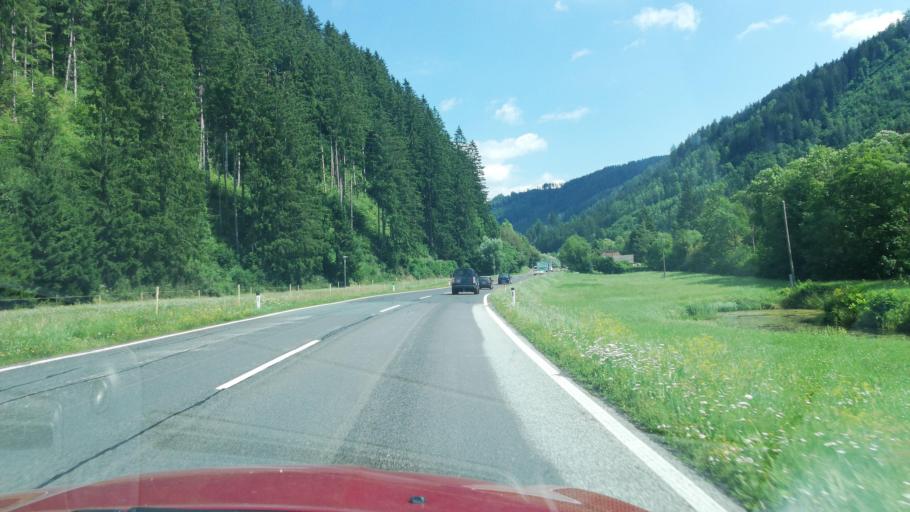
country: AT
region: Styria
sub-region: Politischer Bezirk Murau
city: Durnstein in der Steiermark
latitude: 47.0159
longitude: 14.4089
